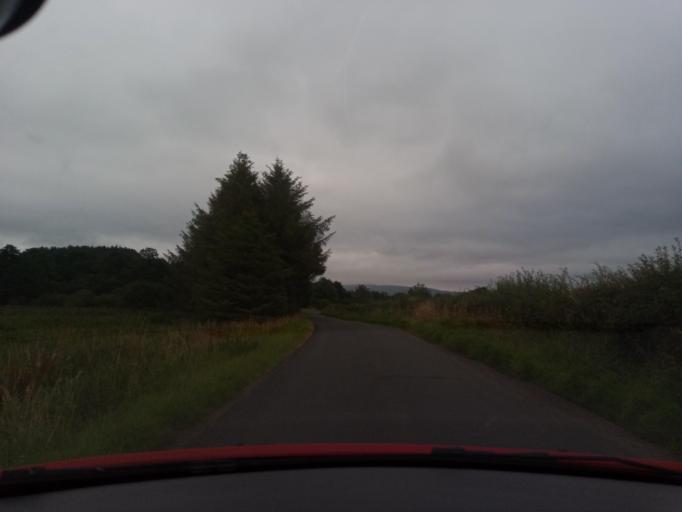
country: GB
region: England
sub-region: Northumberland
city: Otterburn
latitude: 55.3267
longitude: -2.0737
